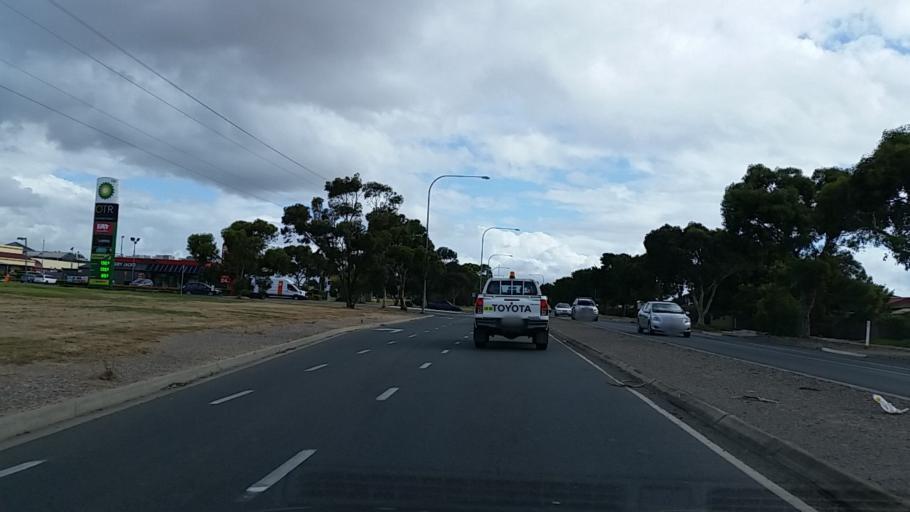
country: AU
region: South Australia
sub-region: Onkaparinga
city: Seaford
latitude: -35.1882
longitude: 138.4774
